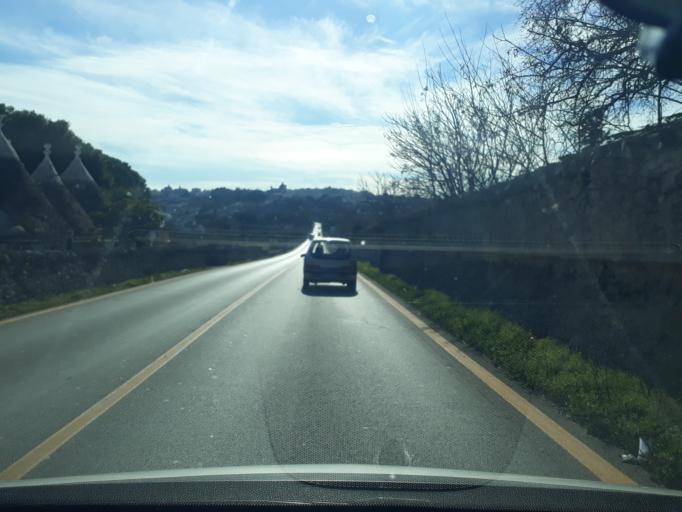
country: IT
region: Apulia
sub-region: Provincia di Taranto
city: Martina Franca
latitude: 40.7190
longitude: 17.3327
